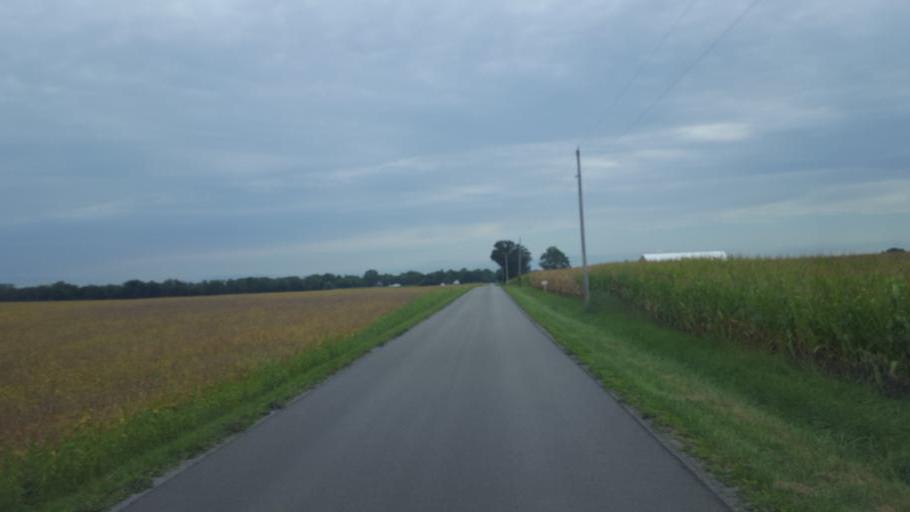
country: US
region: Ohio
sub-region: Wyandot County
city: Upper Sandusky
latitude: 40.7485
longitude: -83.1882
